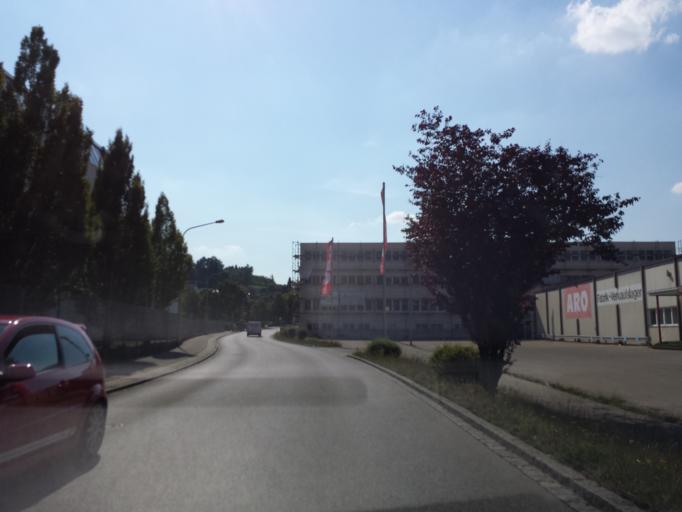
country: DE
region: Bavaria
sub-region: Swabia
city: Krumbach
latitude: 48.2538
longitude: 10.3589
